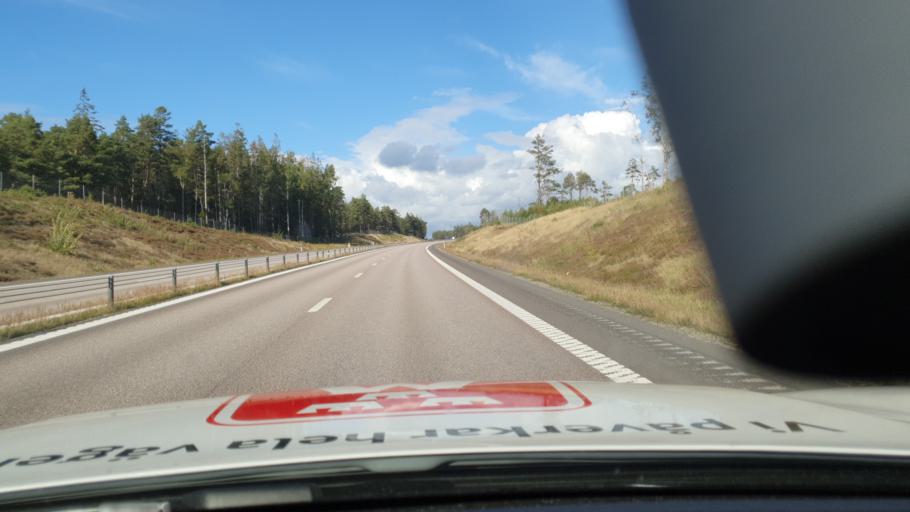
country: SE
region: Vaestra Goetaland
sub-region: Tanums Kommun
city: Tanumshede
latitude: 58.7797
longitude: 11.2742
